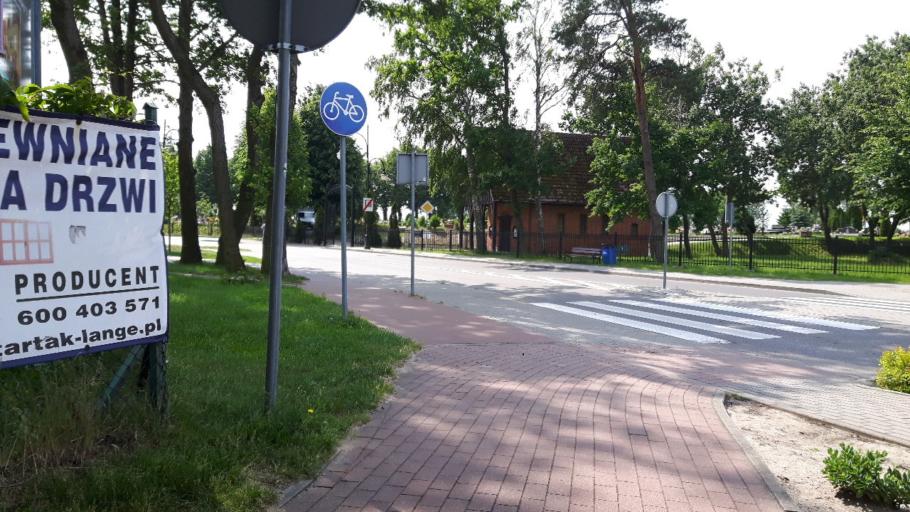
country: PL
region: Pomeranian Voivodeship
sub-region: Powiat leborski
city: Leba
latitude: 54.7509
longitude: 17.5623
